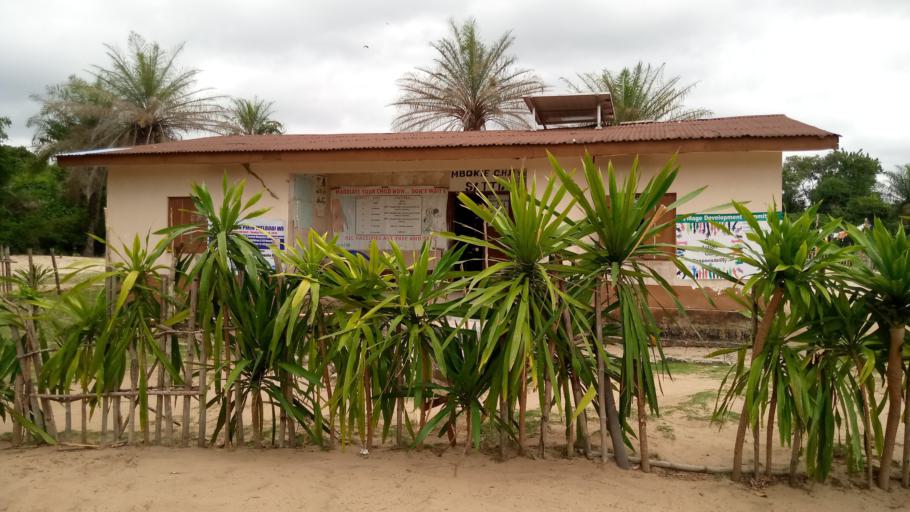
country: SL
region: Southern Province
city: Bonthe
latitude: 7.6370
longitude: -12.6162
